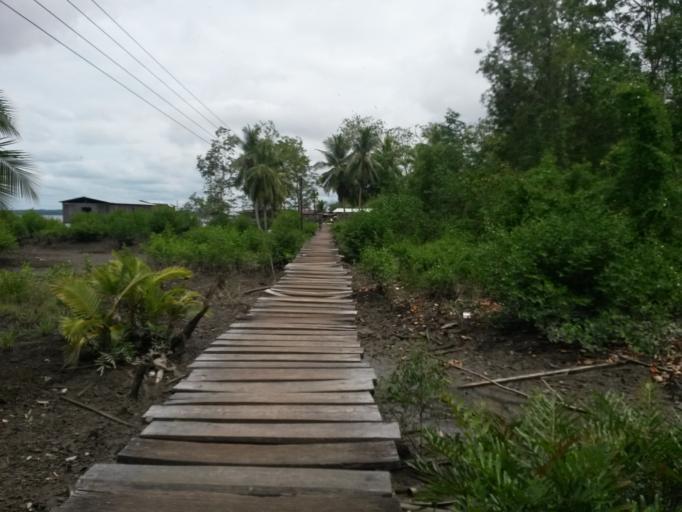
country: CO
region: Cauca
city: Timbiqui
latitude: 2.7313
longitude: -77.7901
